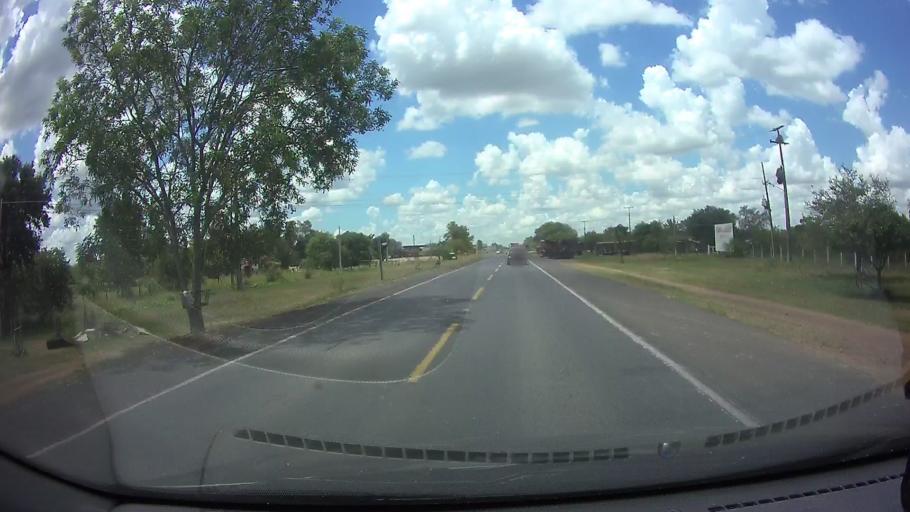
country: PY
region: Presidente Hayes
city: Nanawa
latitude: -25.2191
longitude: -57.6735
